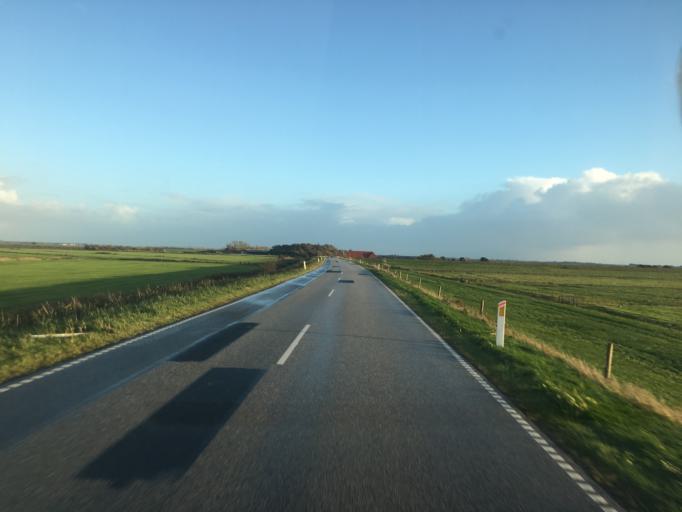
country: DE
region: Schleswig-Holstein
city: Rodenas
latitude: 54.9326
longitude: 8.7174
